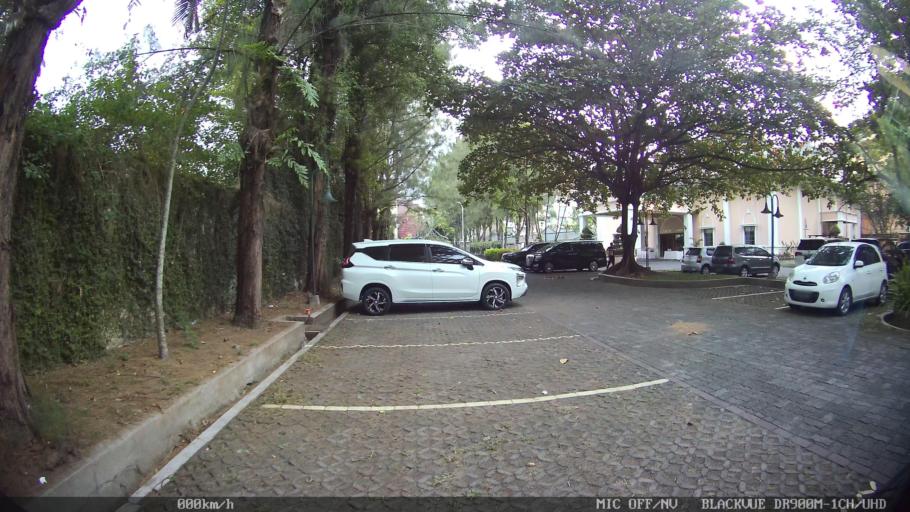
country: ID
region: Daerah Istimewa Yogyakarta
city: Yogyakarta
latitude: -7.7979
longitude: 110.3680
